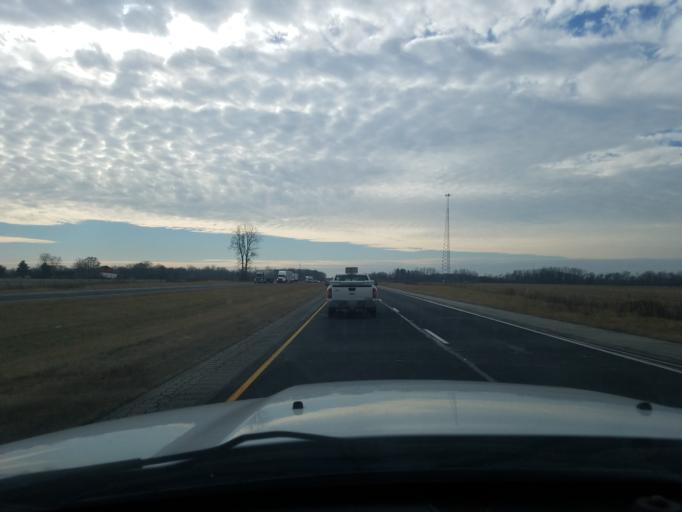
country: US
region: Indiana
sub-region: Huntington County
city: Roanoke
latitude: 40.9094
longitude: -85.3317
